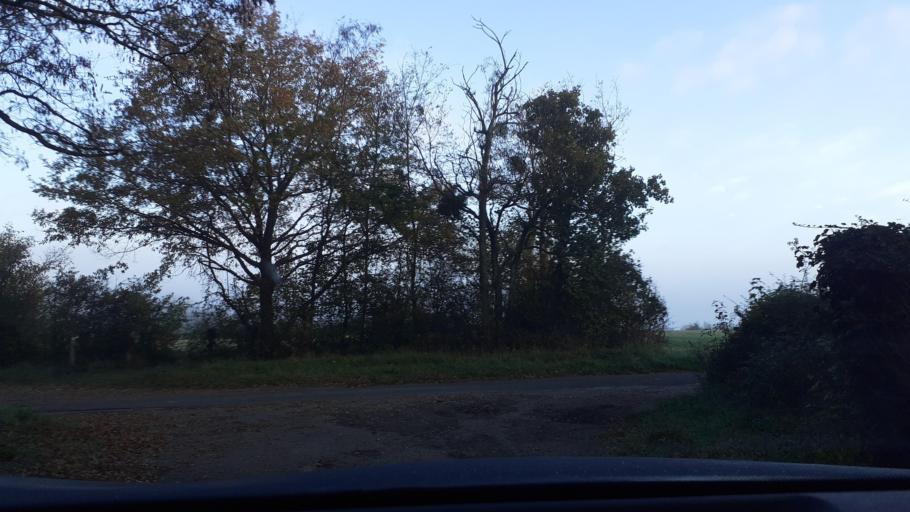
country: FR
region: Rhone-Alpes
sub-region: Departement du Rhone
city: Charnay
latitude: 45.9153
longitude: 4.6674
